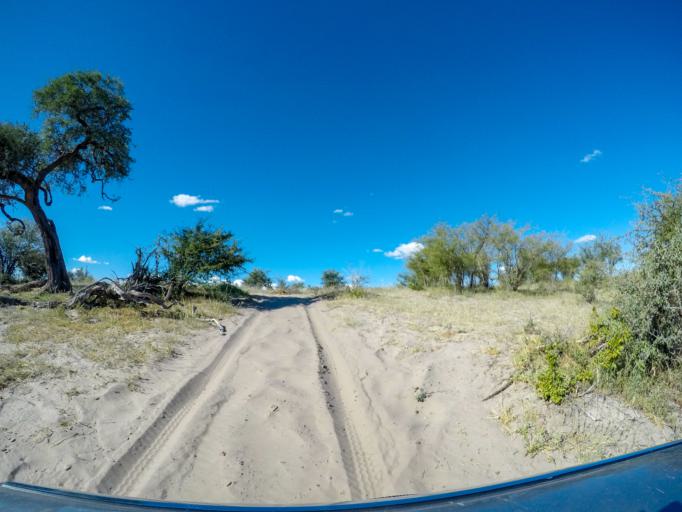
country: BW
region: Central
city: Rakops
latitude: -20.3868
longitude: 24.5056
